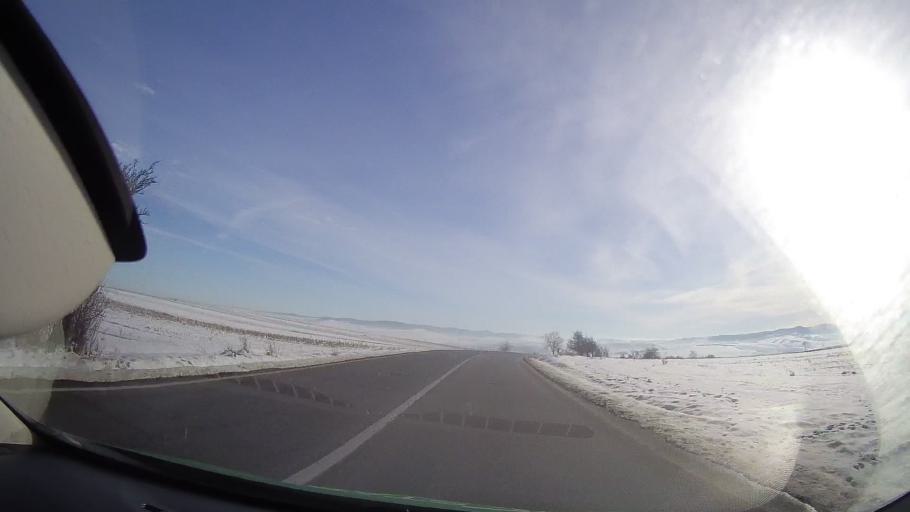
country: RO
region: Neamt
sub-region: Comuna Baltatesti
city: Valea Seaca
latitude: 47.1553
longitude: 26.3237
